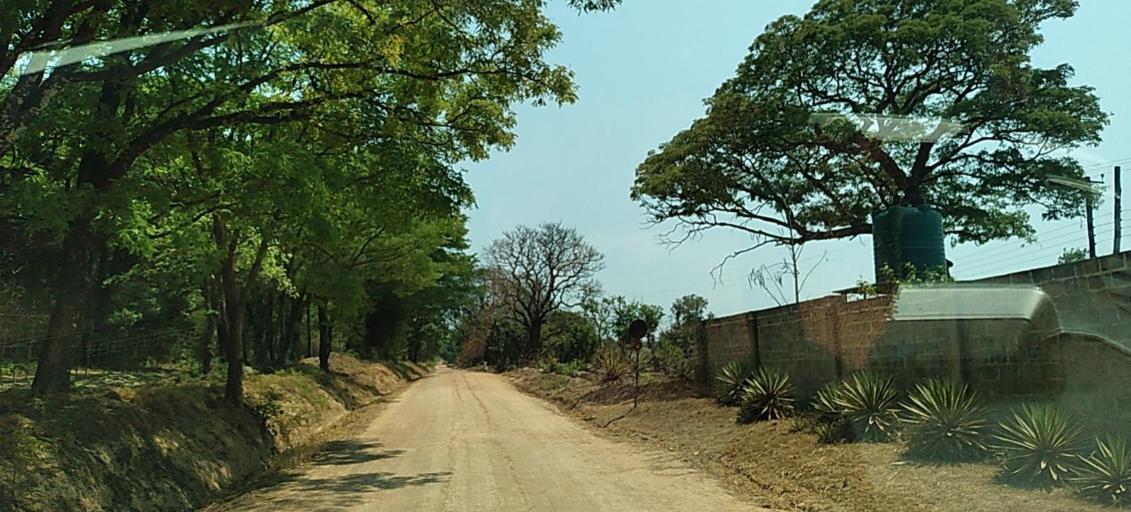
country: ZM
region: Copperbelt
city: Chambishi
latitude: -12.6069
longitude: 27.9534
